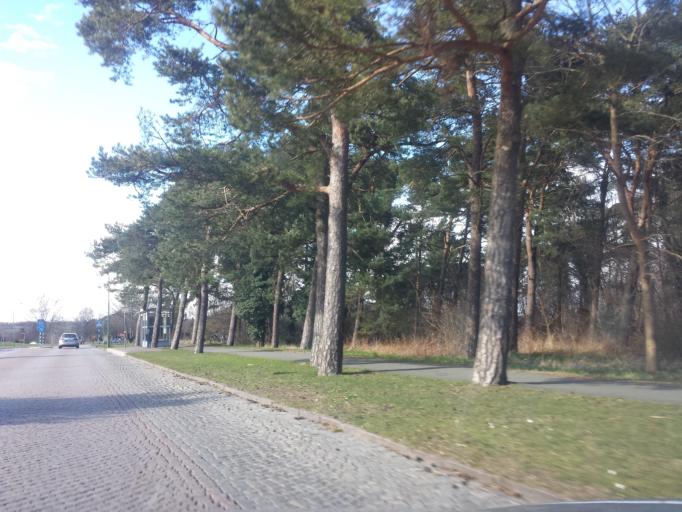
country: SE
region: Skane
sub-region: Simrishamns Kommun
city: Simrishamn
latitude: 55.5617
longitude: 14.3394
